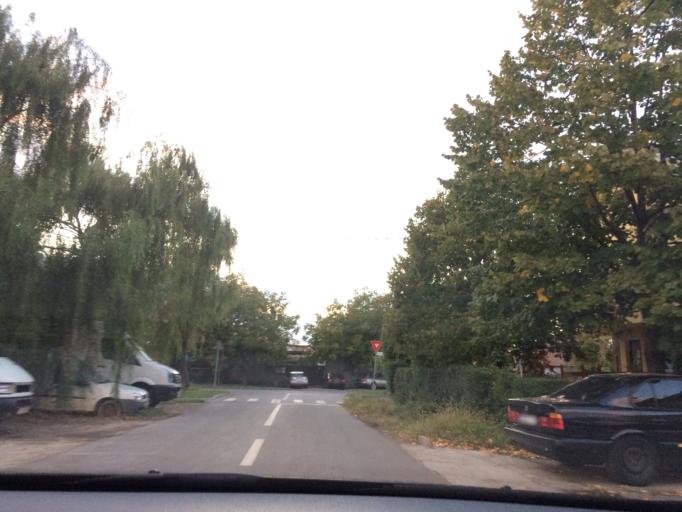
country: RO
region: Timis
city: Timisoara
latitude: 45.7659
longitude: 21.1962
